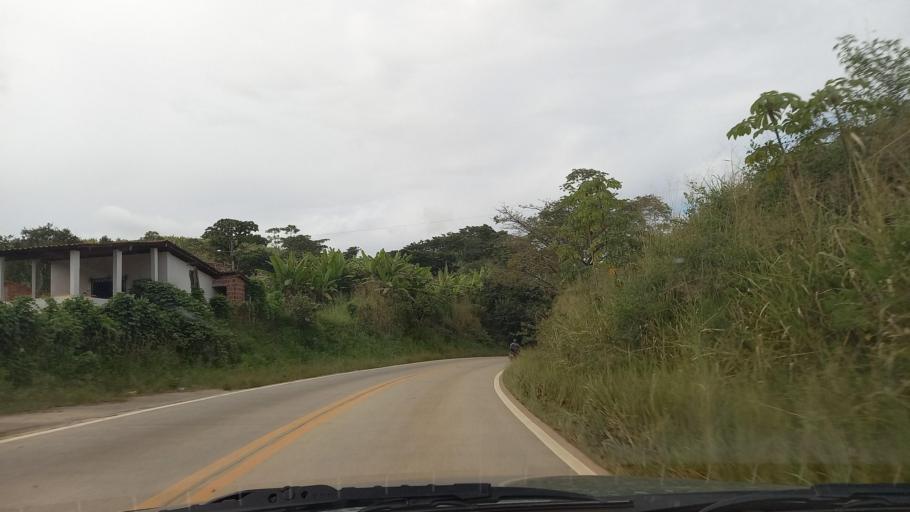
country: BR
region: Pernambuco
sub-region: Maraial
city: Maraial
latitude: -8.7548
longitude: -35.8471
